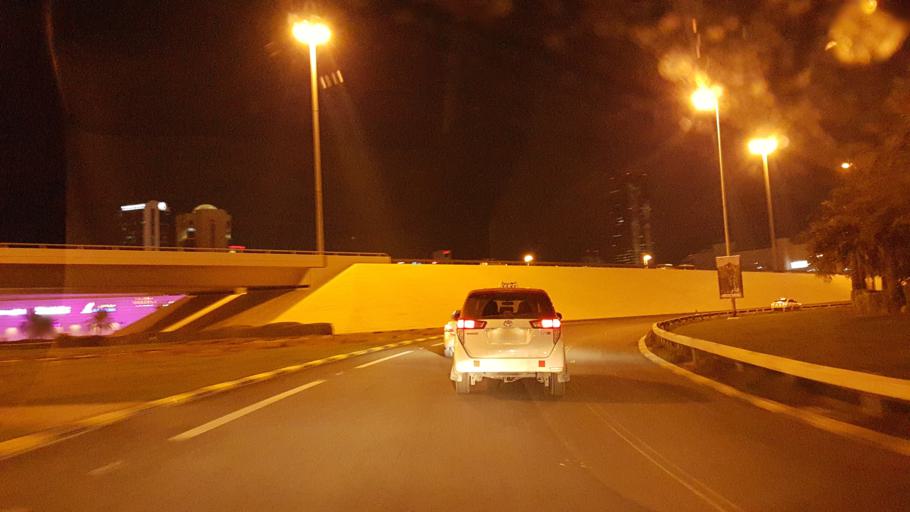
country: BH
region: Manama
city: Jidd Hafs
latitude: 26.2300
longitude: 50.5355
